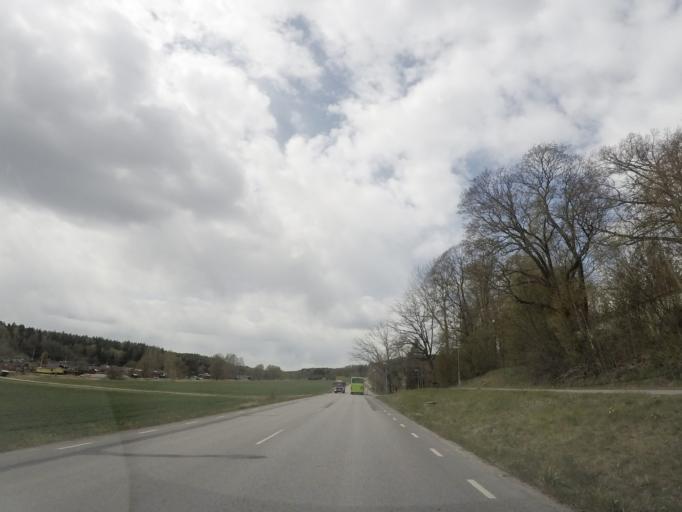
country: SE
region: Soedermanland
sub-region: Nykopings Kommun
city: Nykoping
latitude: 58.7411
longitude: 16.9401
